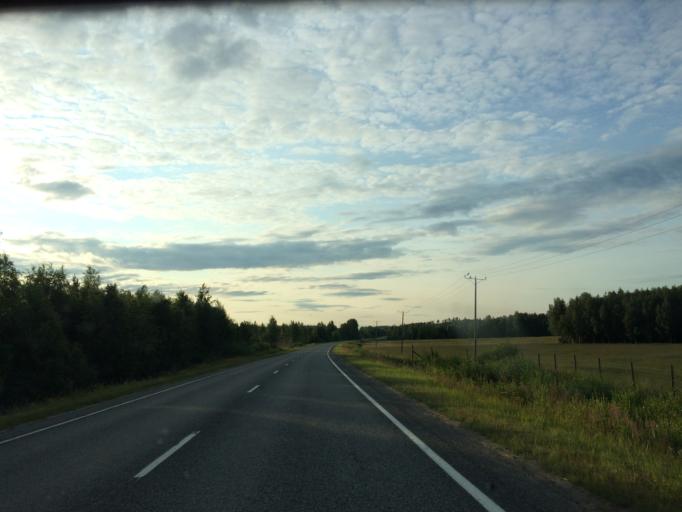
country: FI
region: Haeme
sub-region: Haemeenlinna
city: Janakkala
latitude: 60.8625
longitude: 24.5864
